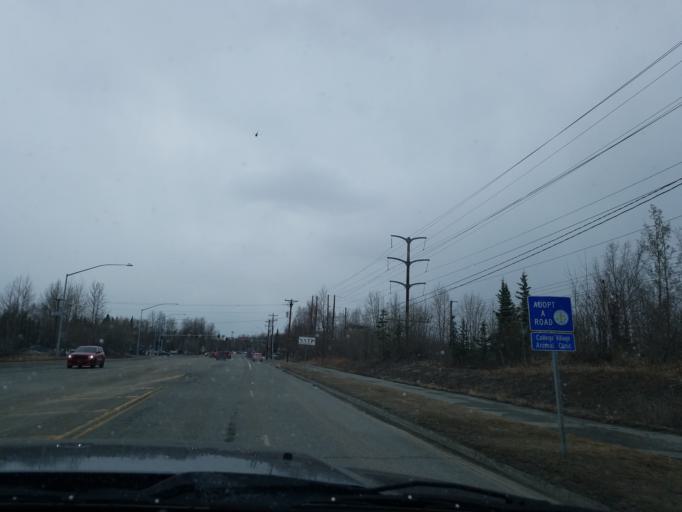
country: US
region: Alaska
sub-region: Anchorage Municipality
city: Anchorage
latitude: 61.1791
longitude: -149.8082
